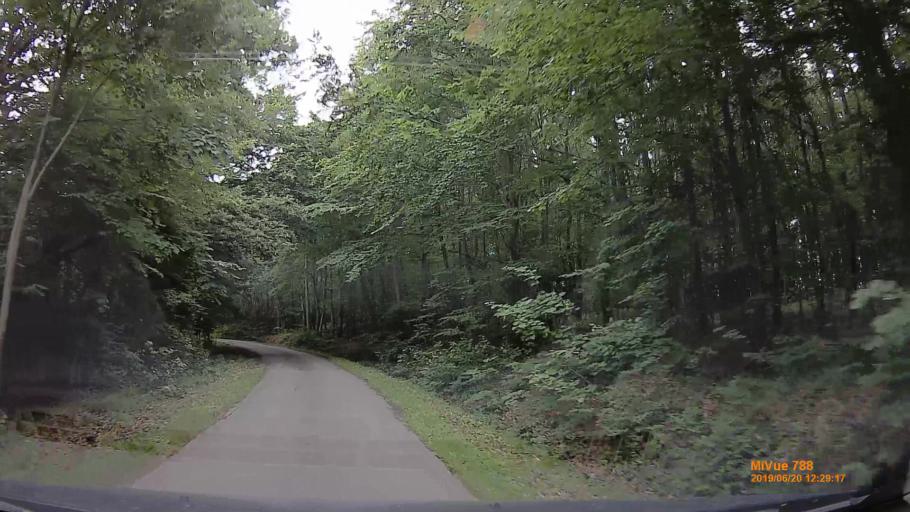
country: HU
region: Baranya
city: Hosszuheteny
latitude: 46.2043
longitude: 18.3527
